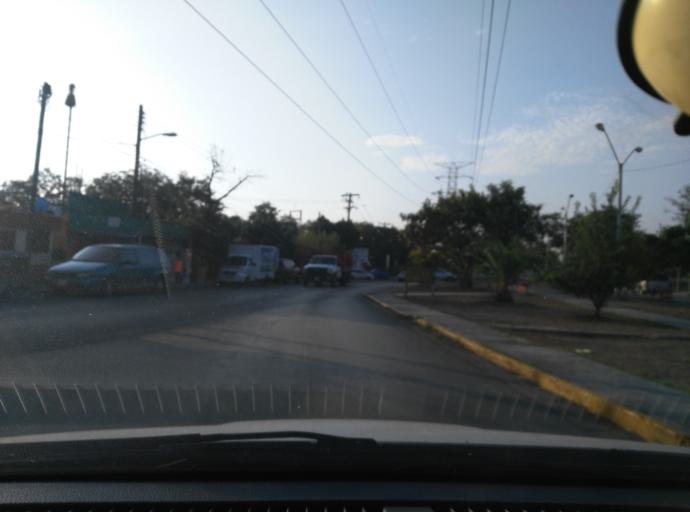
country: MX
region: Nuevo Leon
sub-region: San Nicolas de los Garza
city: San Nicolas de los Garza
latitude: 25.7571
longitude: -100.2490
